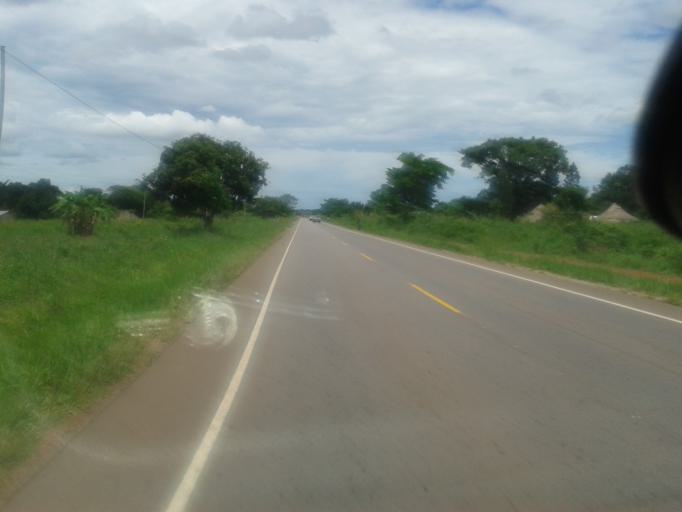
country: UG
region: Western Region
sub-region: Kiryandongo District
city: Masindi Port
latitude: 1.7223
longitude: 32.0266
